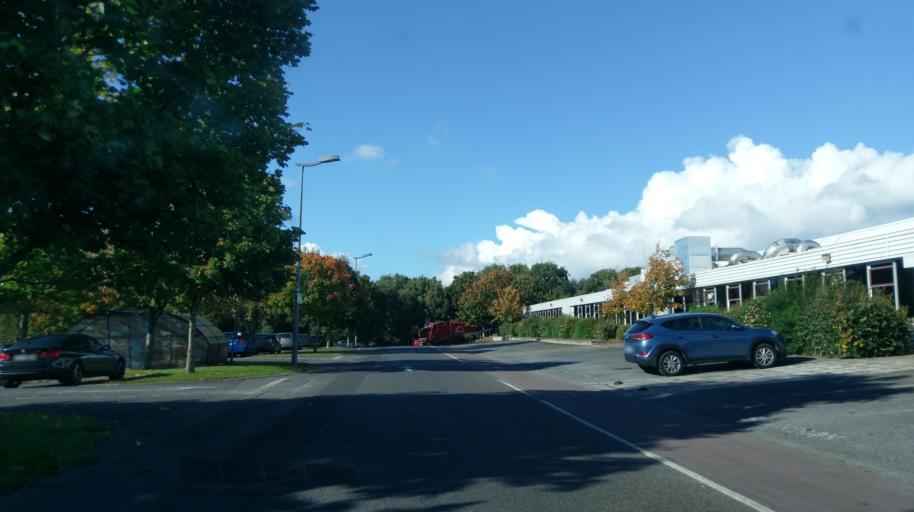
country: IE
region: Connaught
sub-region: County Galway
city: Gaillimh
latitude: 53.2858
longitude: -9.0286
